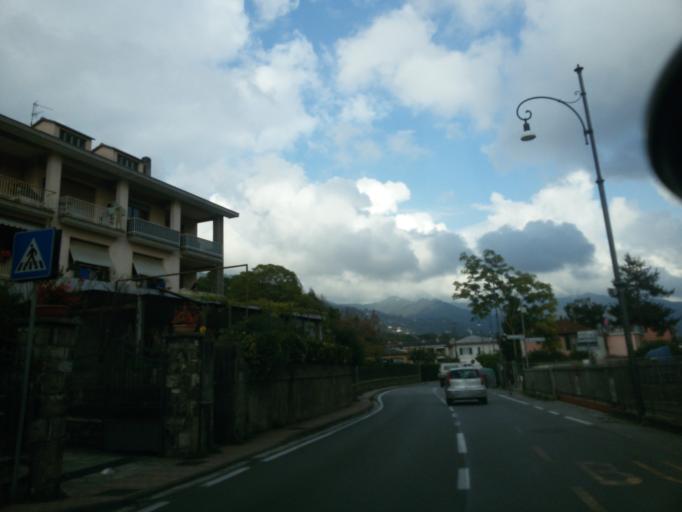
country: IT
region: Liguria
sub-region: Provincia di Genova
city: Santa Margherita Ligure
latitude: 44.3577
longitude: 9.1966
